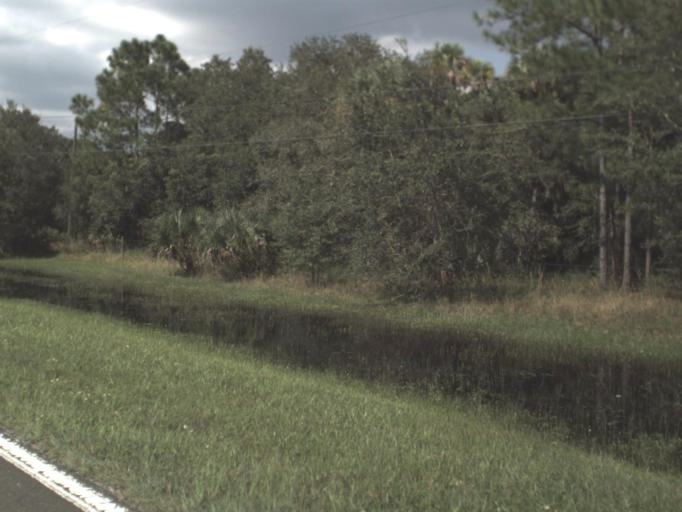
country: US
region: Florida
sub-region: Sarasota County
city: Plantation
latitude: 27.0744
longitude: -82.3272
